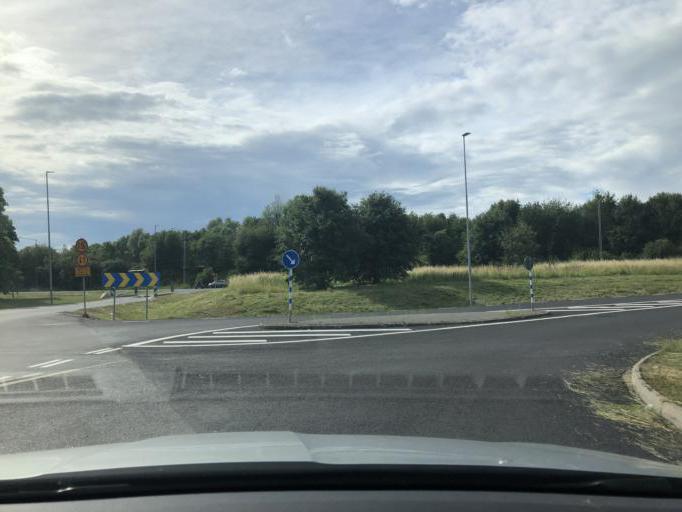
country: SE
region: Stockholm
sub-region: Botkyrka Kommun
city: Fittja
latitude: 59.2476
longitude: 17.8486
